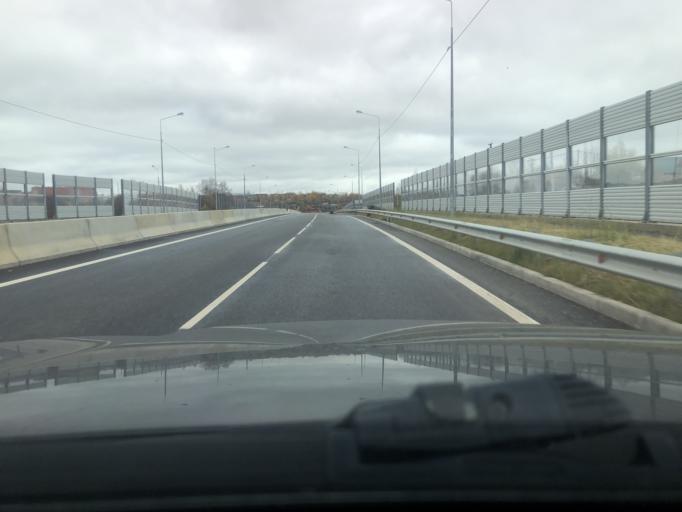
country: RU
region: Moskovskaya
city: Sergiyev Posad
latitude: 56.3361
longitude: 38.1119
